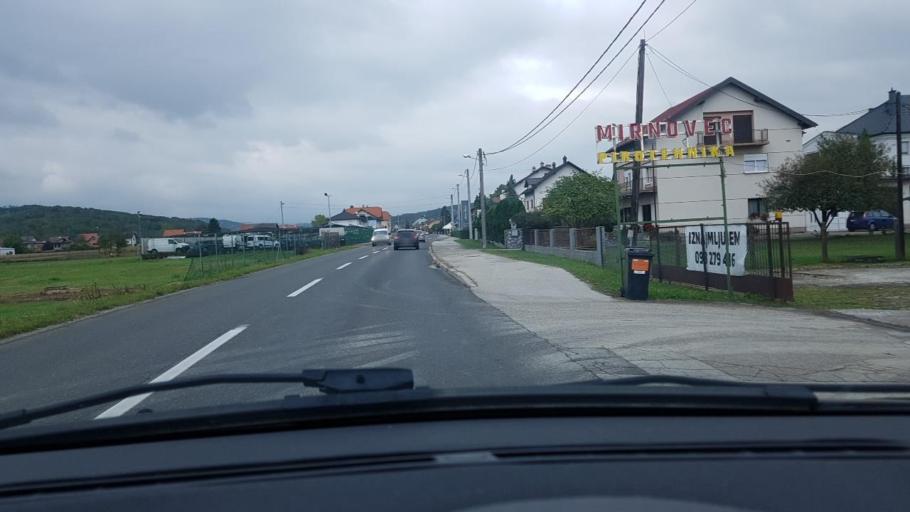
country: HR
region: Grad Zagreb
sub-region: Sesvete
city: Sesvete
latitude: 45.8504
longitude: 16.1113
